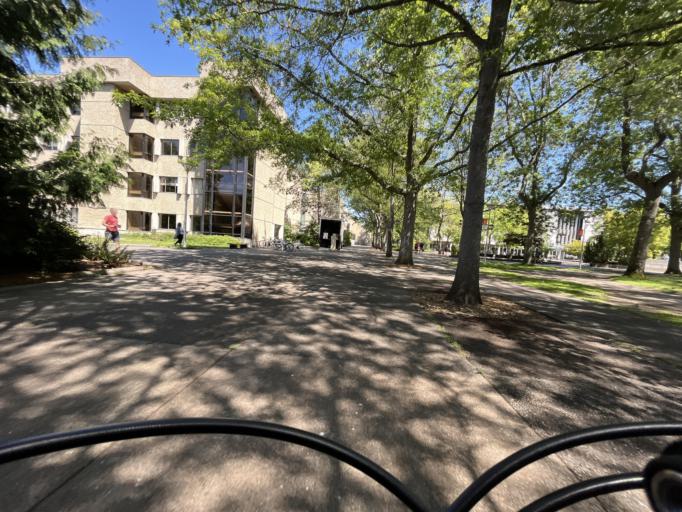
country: CA
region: British Columbia
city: Oak Bay
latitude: 48.4638
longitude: -123.3113
